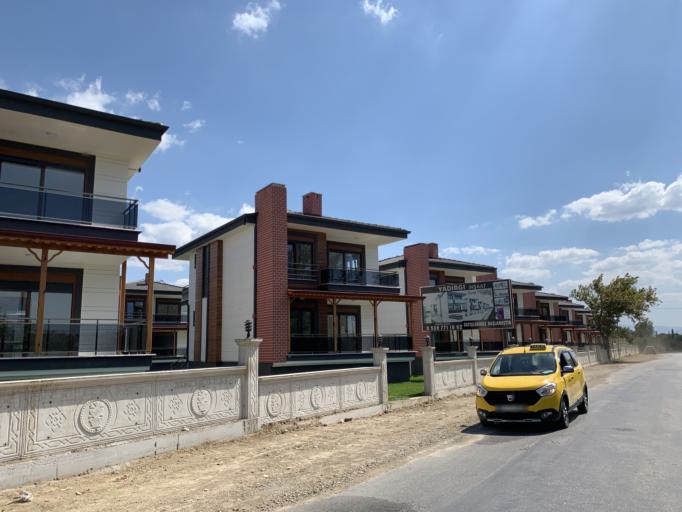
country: TR
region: Balikesir
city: Altinoluk
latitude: 39.5656
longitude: 26.8367
